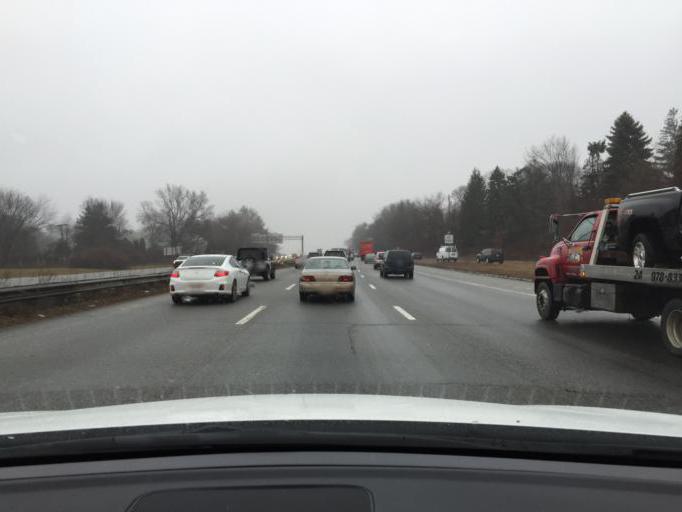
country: US
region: Massachusetts
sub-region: Norfolk County
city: Needham
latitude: 42.3154
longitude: -71.2331
